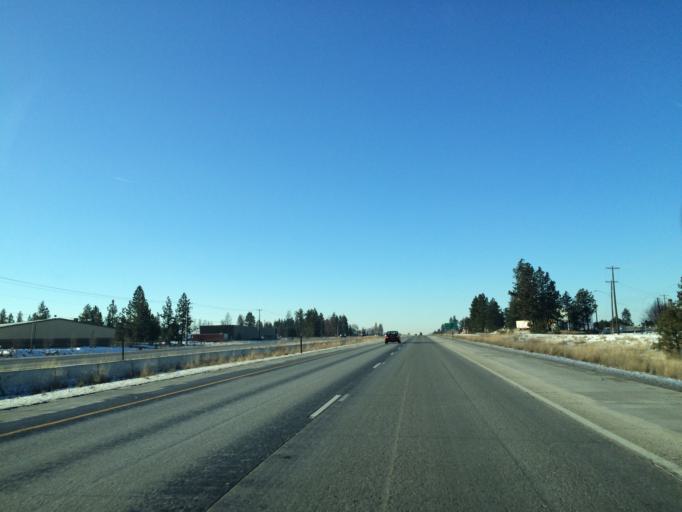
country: US
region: Washington
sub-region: Spokane County
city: Airway Heights
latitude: 47.6142
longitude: -117.5136
